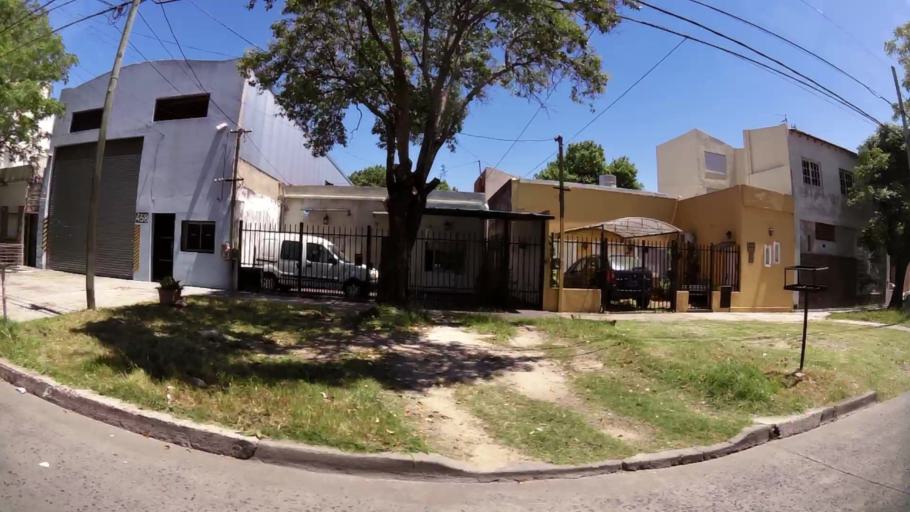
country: AR
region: Buenos Aires
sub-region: Partido de General San Martin
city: General San Martin
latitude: -34.5943
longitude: -58.5285
